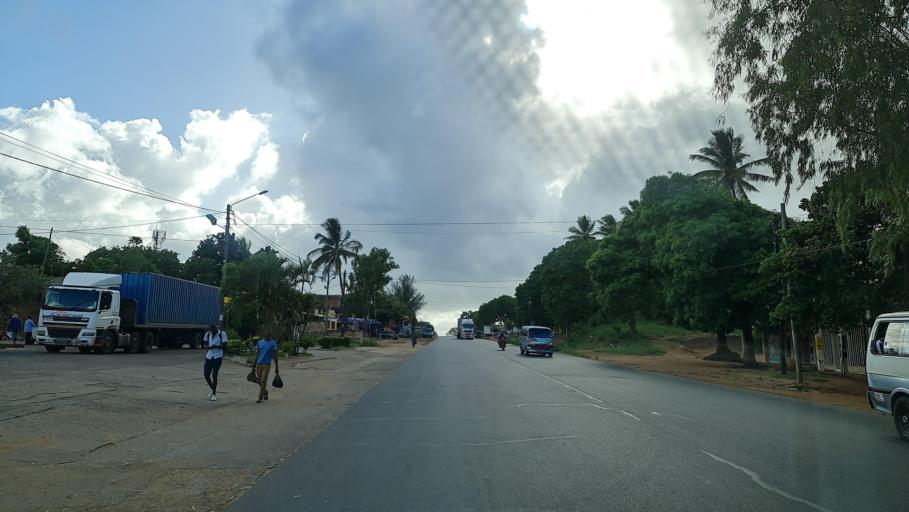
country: MZ
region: Gaza
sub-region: Xai-Xai District
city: Xai-Xai
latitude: -25.0572
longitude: 33.6804
